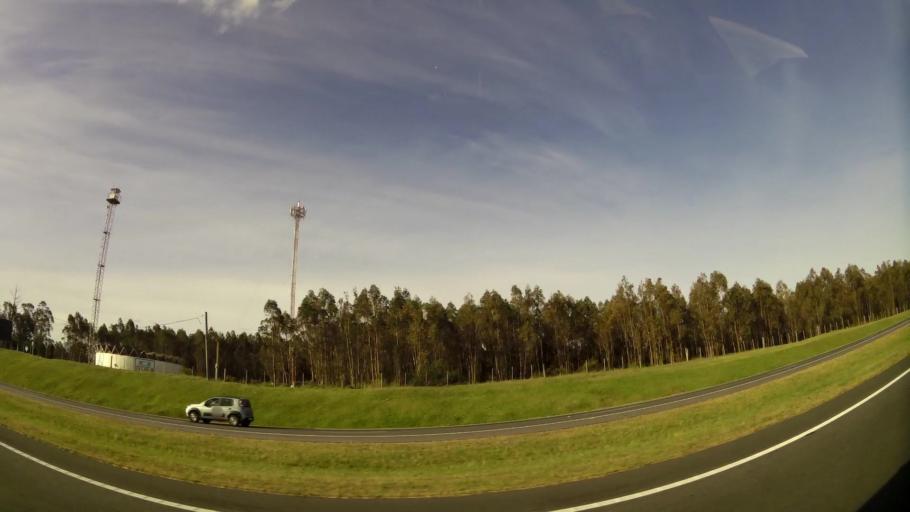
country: UY
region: Canelones
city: La Floresta
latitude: -34.7817
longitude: -55.5463
